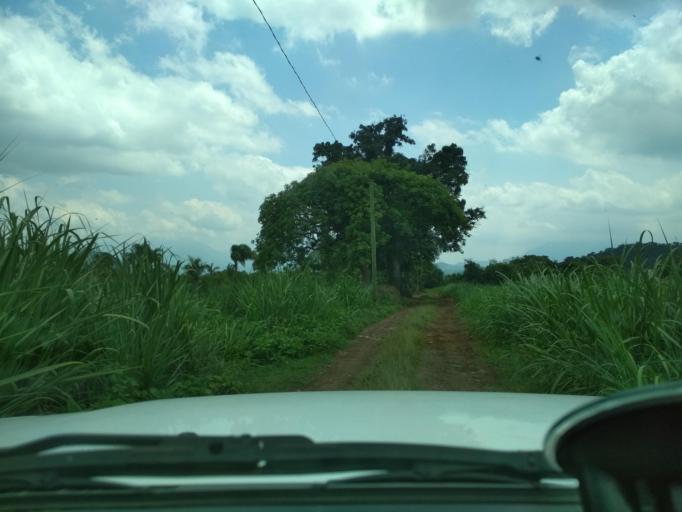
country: MX
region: Veracruz
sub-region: Fortin
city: Monte Salas
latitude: 18.9313
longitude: -97.0187
